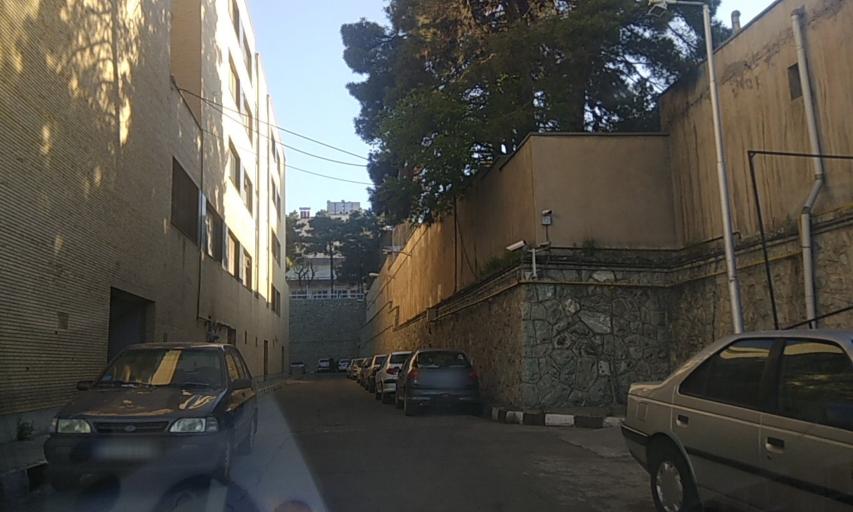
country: IR
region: Tehran
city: Tajrish
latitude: 35.7688
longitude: 51.4099
